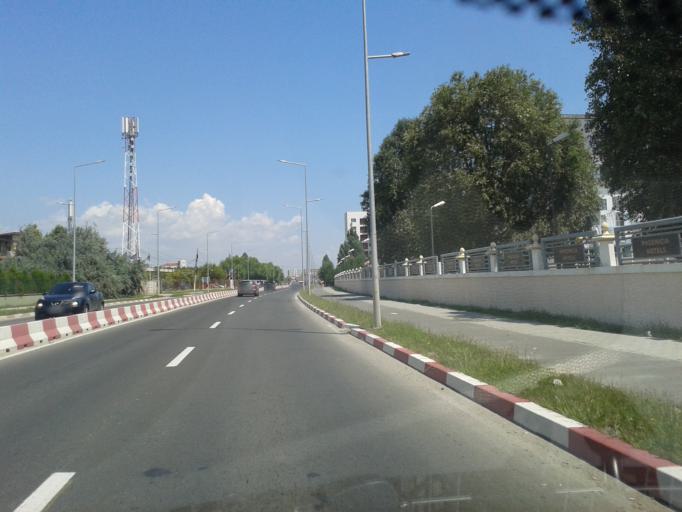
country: RO
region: Constanta
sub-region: Comuna Navodari
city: Navodari
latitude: 44.2793
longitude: 28.6175
